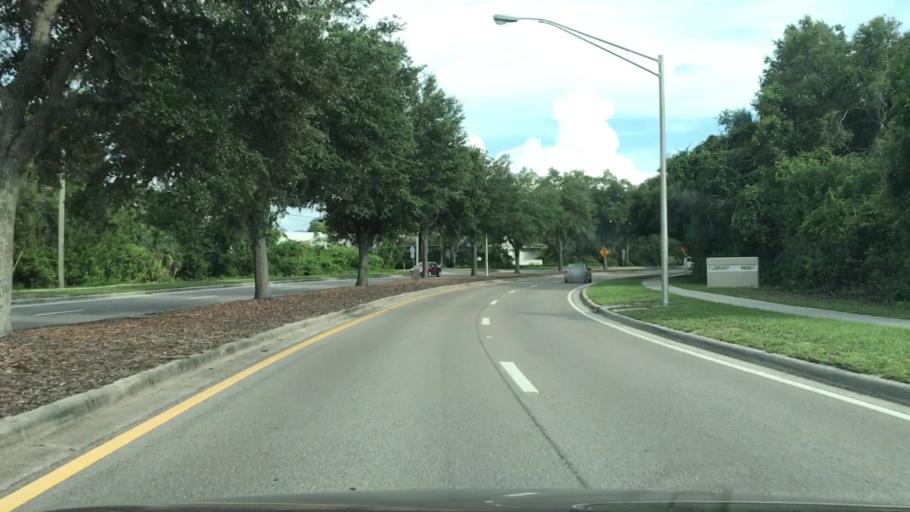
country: US
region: Florida
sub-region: Sarasota County
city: Venice Gardens
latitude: 27.0573
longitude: -82.3948
